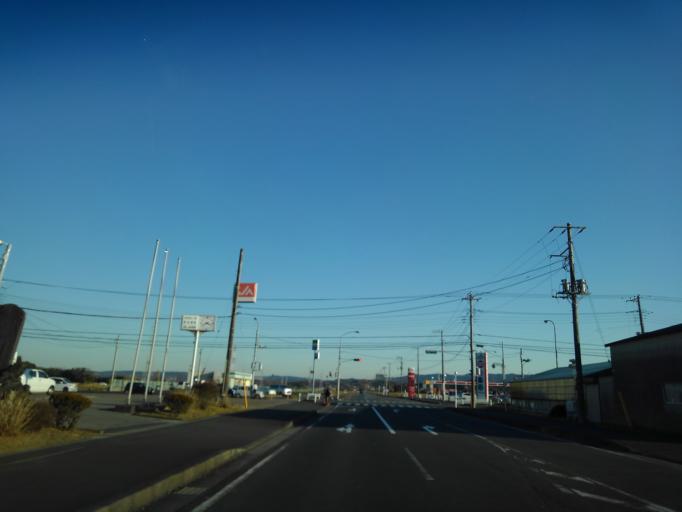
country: JP
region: Chiba
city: Kimitsu
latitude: 35.3199
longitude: 139.9047
